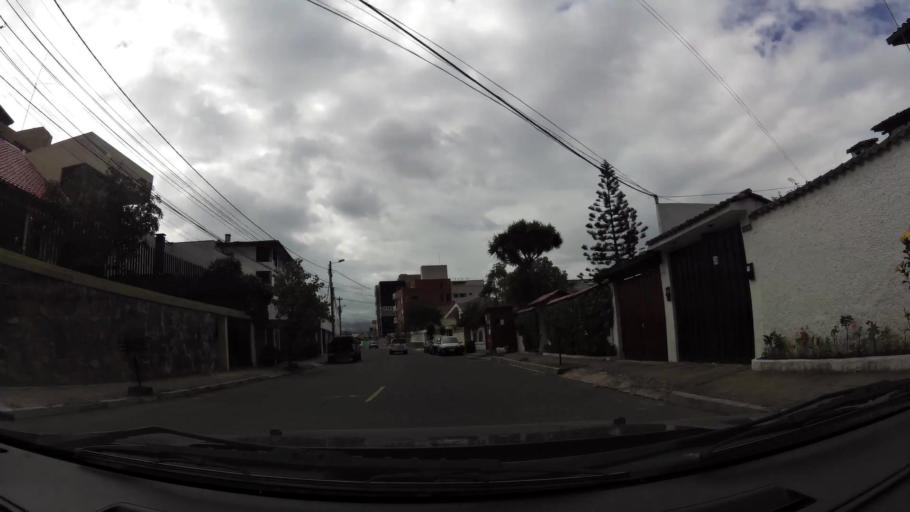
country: EC
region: Pichincha
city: Quito
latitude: -0.1508
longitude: -78.4968
